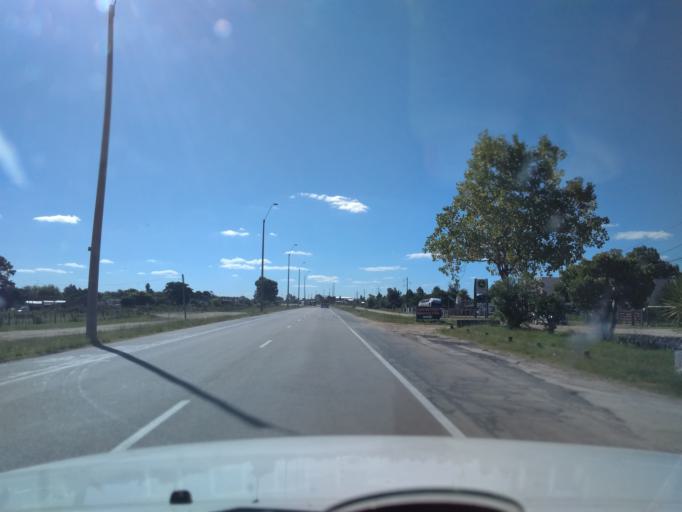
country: UY
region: Florida
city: Florida
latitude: -34.0817
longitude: -56.2168
